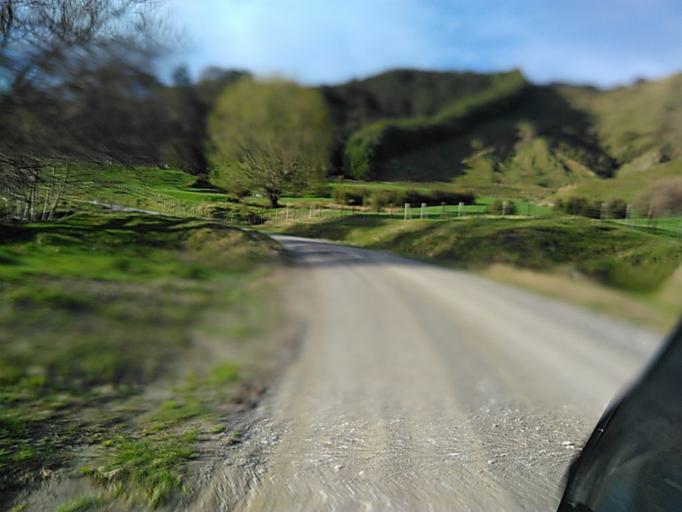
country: NZ
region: Gisborne
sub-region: Gisborne District
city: Gisborne
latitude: -38.5975
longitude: 178.0695
